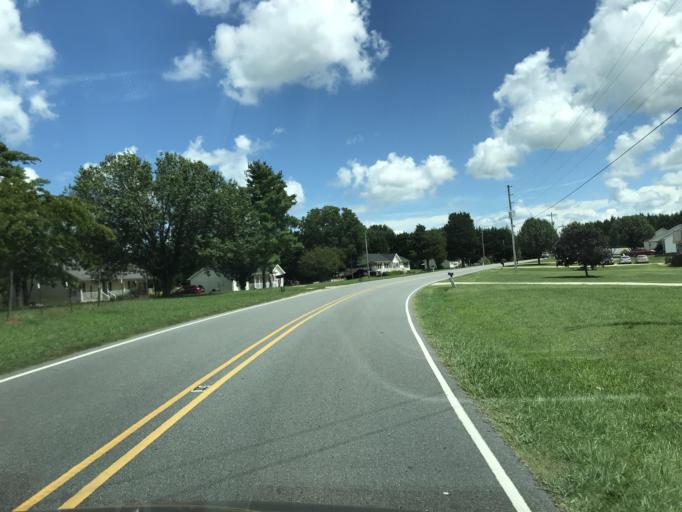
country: US
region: North Carolina
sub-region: Lincoln County
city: Lincolnton
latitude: 35.5046
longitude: -81.2116
